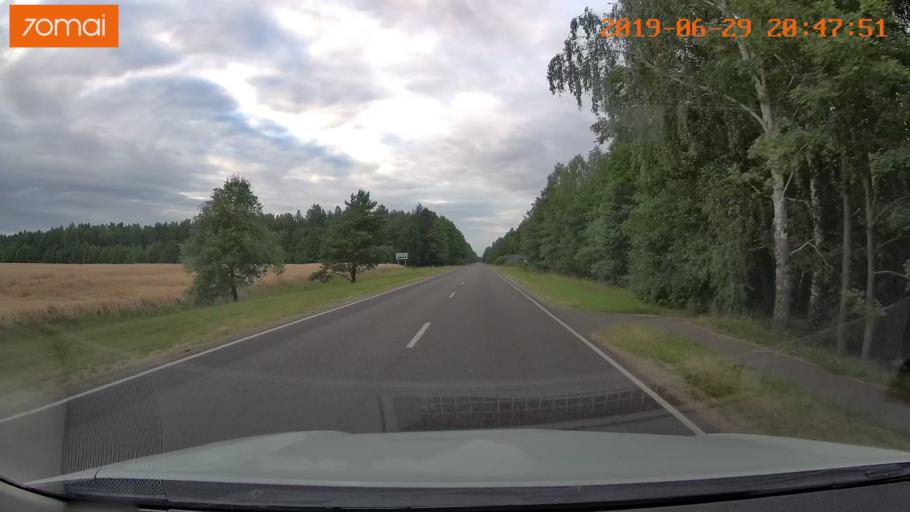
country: BY
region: Brest
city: Hantsavichy
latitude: 52.6430
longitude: 26.3164
